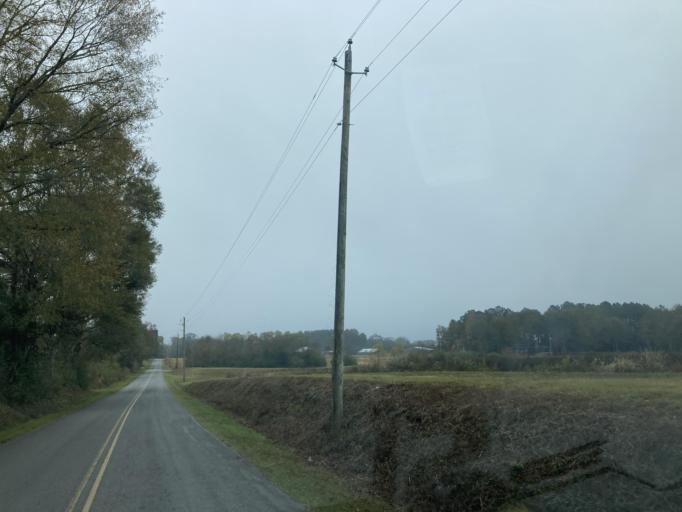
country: US
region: Mississippi
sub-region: Lamar County
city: Lumberton
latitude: 30.9966
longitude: -89.4015
